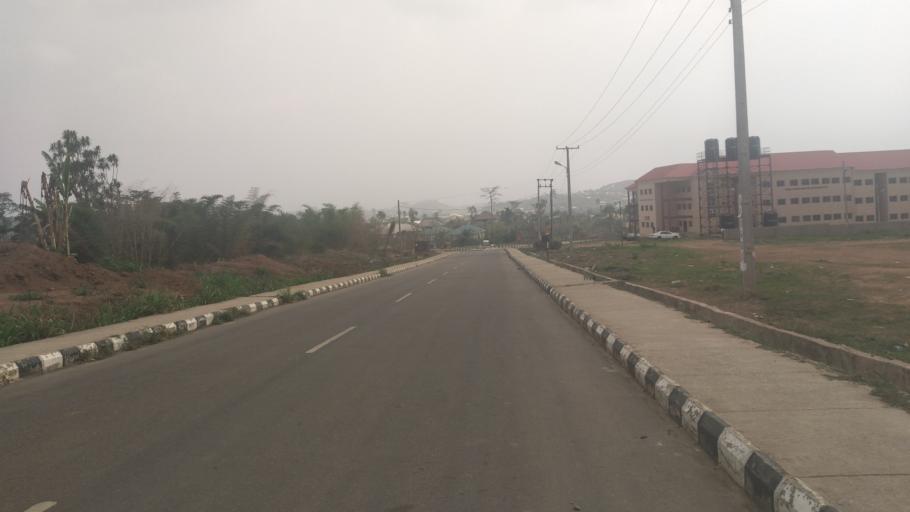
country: NG
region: Ondo
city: Ilare
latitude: 7.2964
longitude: 5.1356
